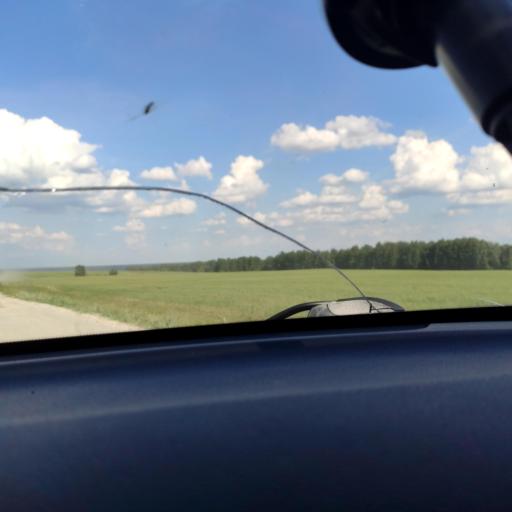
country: RU
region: Tatarstan
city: Verkhniy Uslon
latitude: 55.6431
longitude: 48.9096
